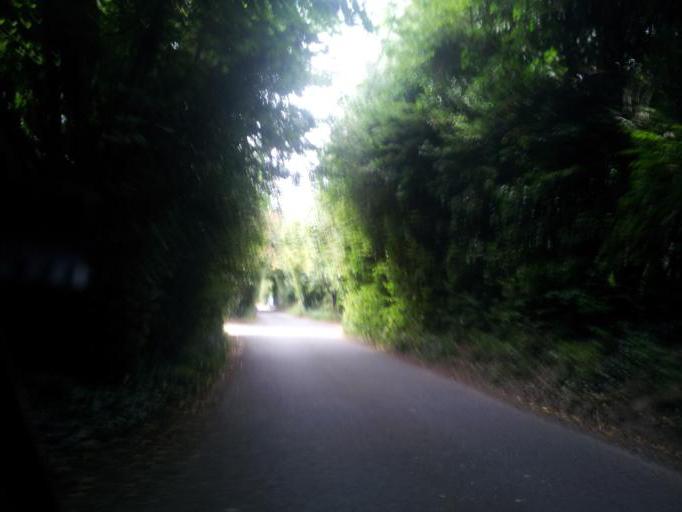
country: GB
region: England
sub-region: Kent
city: Meopham
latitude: 51.3853
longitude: 0.3859
